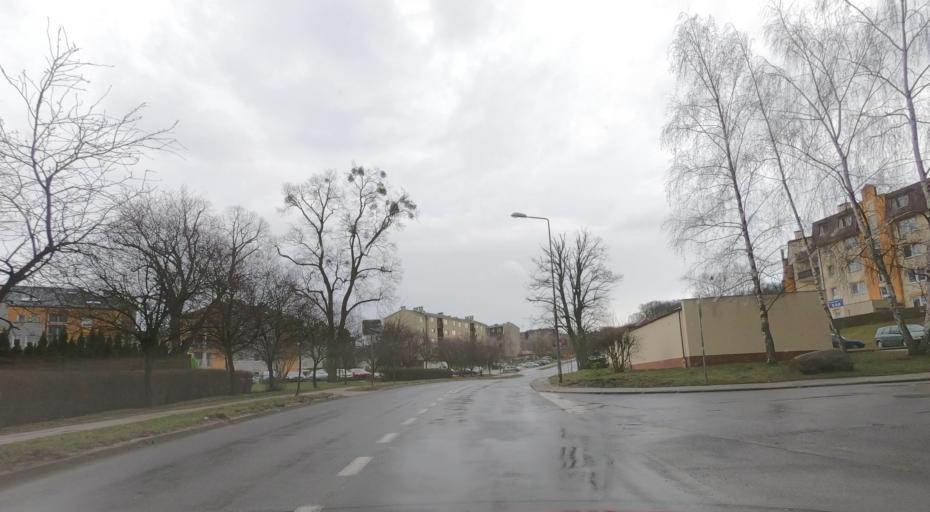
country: PL
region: West Pomeranian Voivodeship
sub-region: Szczecin
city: Szczecin
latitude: 53.3682
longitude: 14.6461
